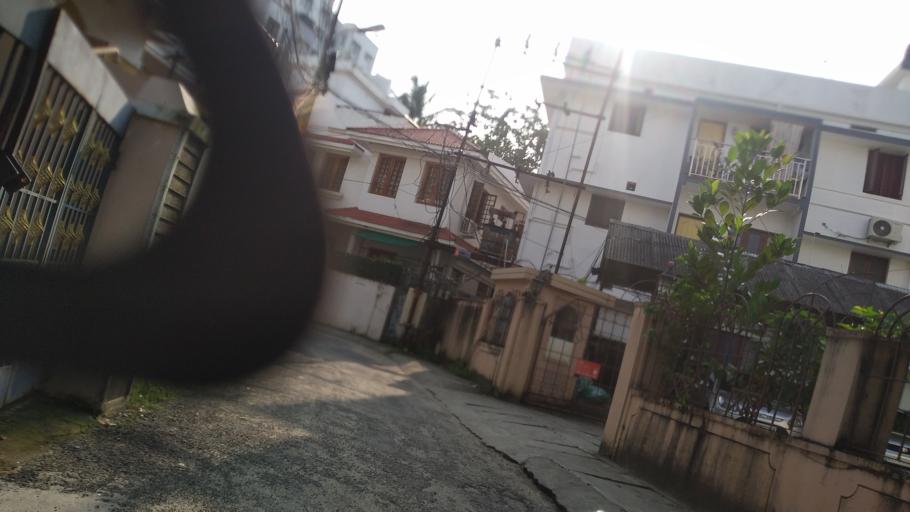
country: IN
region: Kerala
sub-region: Ernakulam
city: Cochin
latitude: 9.9990
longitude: 76.2942
